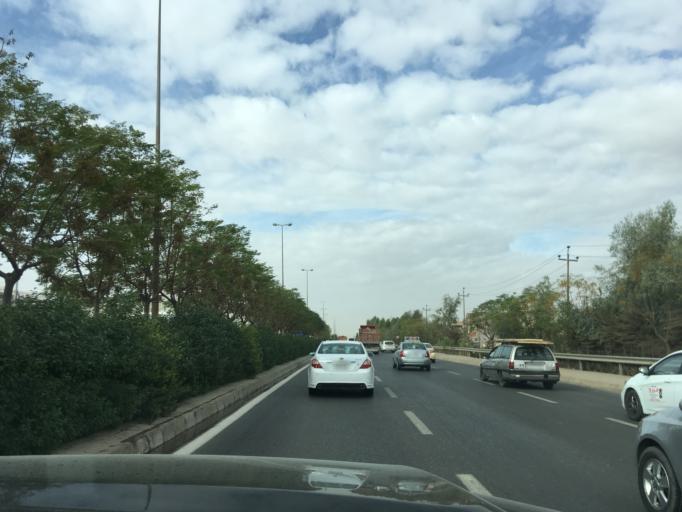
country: IQ
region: Dahuk
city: Dihok
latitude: 36.8470
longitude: 43.0246
